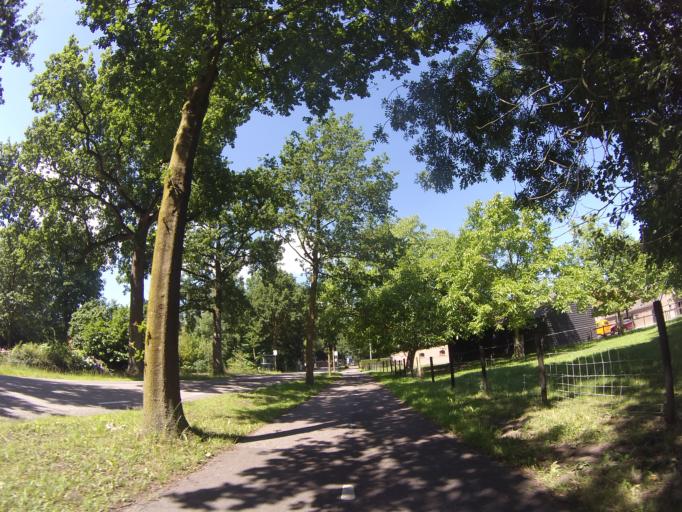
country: NL
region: Utrecht
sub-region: Stichtse Vecht
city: Spechtenkamp
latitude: 52.1188
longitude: 4.9988
